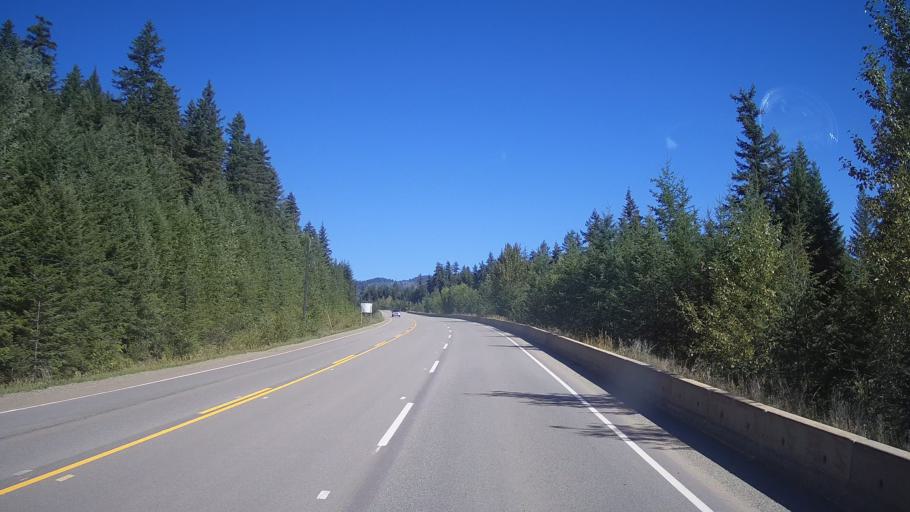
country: CA
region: British Columbia
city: Kamloops
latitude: 51.4612
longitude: -120.2303
